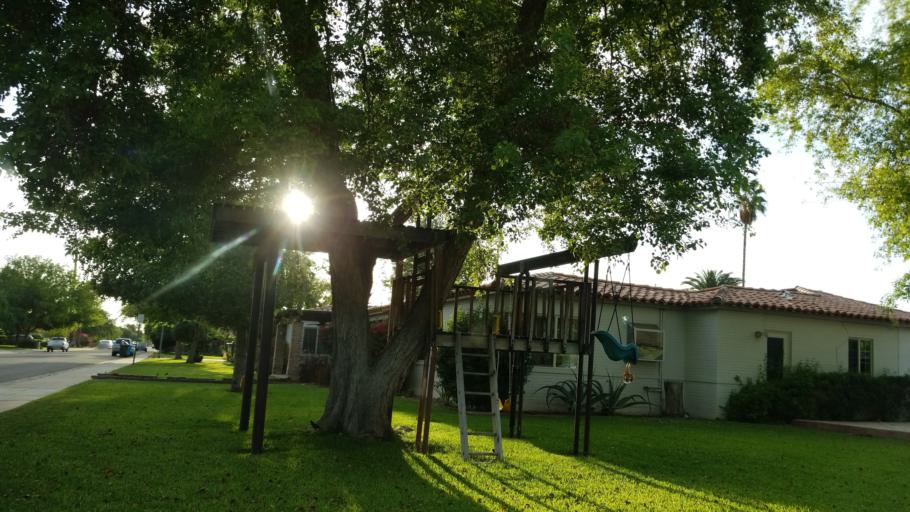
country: US
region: Arizona
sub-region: Maricopa County
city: Phoenix
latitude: 33.4796
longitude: -112.0889
